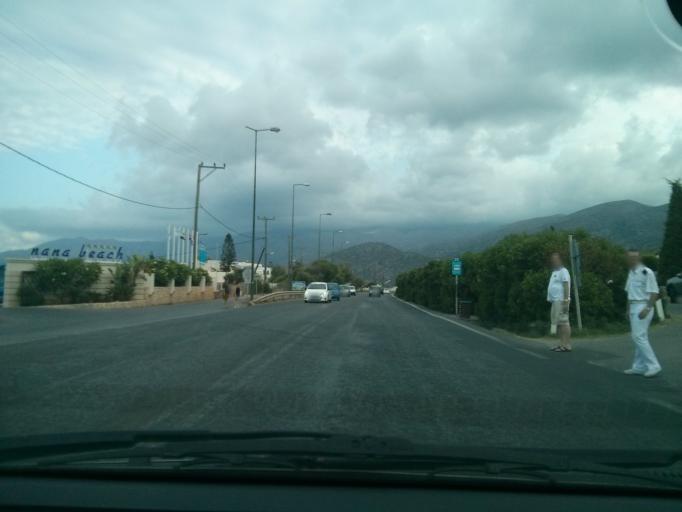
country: GR
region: Crete
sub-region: Nomos Irakleiou
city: Stalis
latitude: 35.3023
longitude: 25.4196
